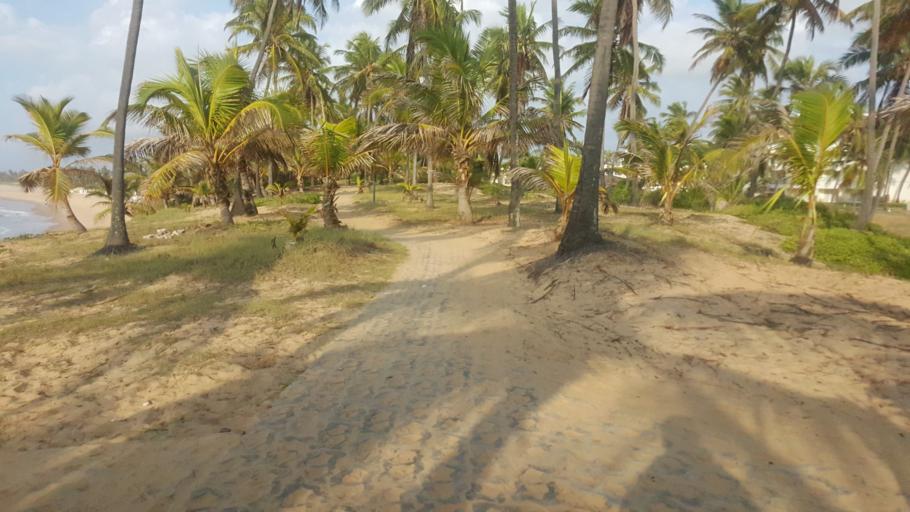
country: BR
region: Bahia
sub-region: Mata De Sao Joao
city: Mata de Sao Joao
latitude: -12.4423
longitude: -37.9206
